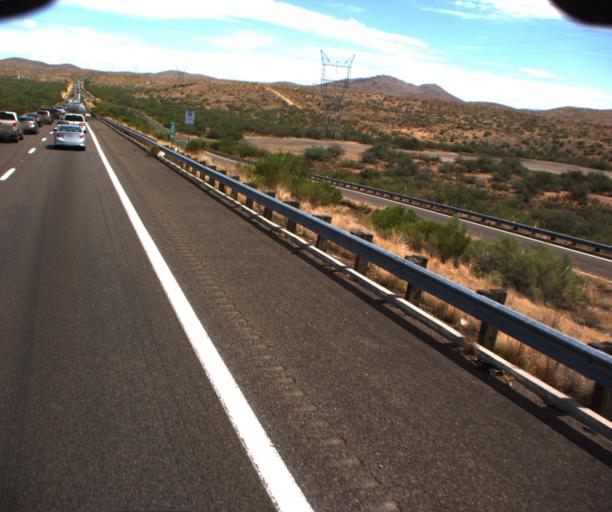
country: US
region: Arizona
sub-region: Yavapai County
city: Cordes Lakes
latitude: 34.2351
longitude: -112.1115
